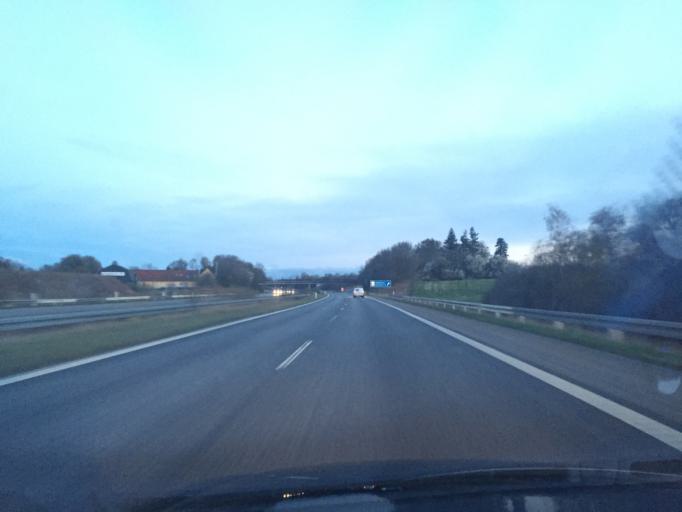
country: DK
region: Capital Region
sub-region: Fredensborg Kommune
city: Kokkedal
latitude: 55.9139
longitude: 12.4712
